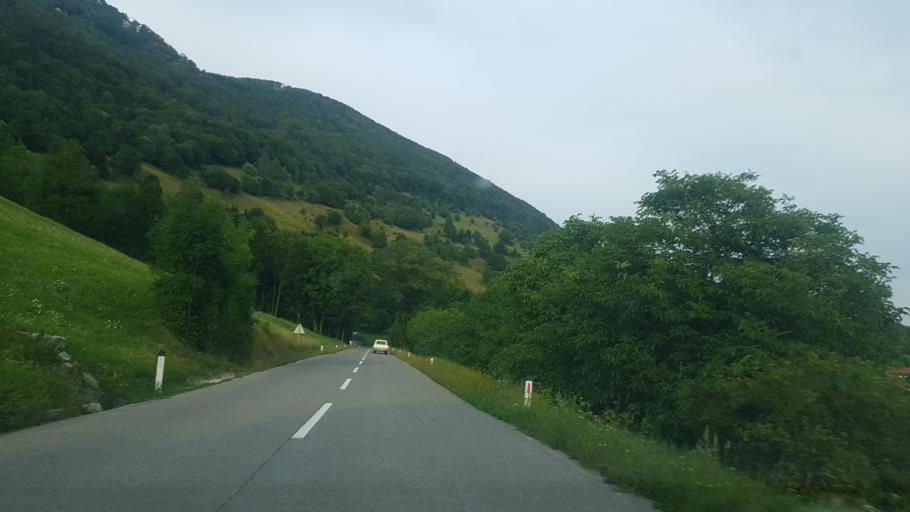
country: SI
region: Vipava
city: Vipava
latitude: 45.8668
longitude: 14.0550
